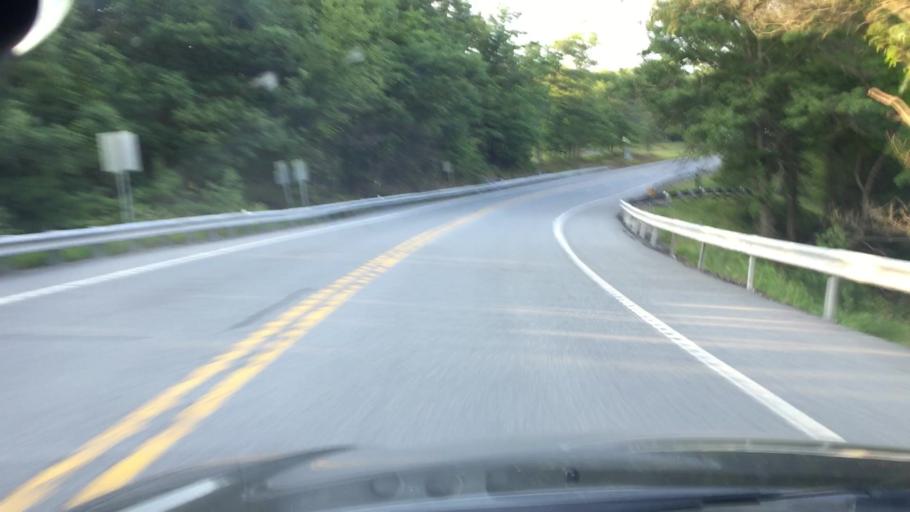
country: US
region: Pennsylvania
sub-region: Carbon County
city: Nesquehoning
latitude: 40.8713
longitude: -75.7900
